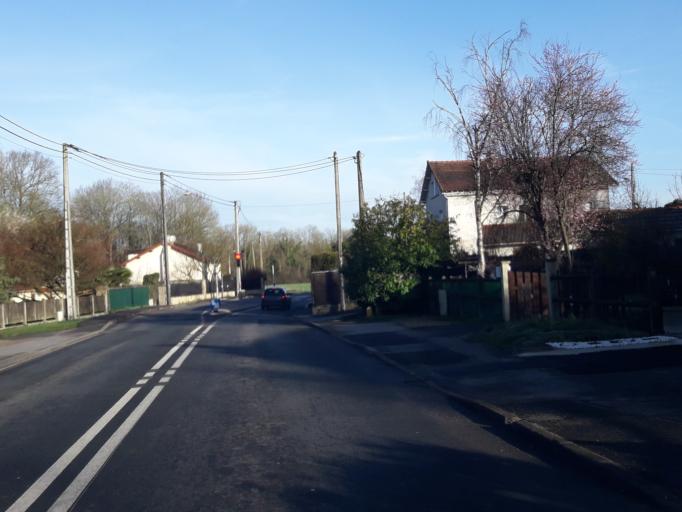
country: FR
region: Ile-de-France
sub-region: Departement de l'Essonne
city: Saint-Vrain
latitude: 48.5306
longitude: 2.3398
